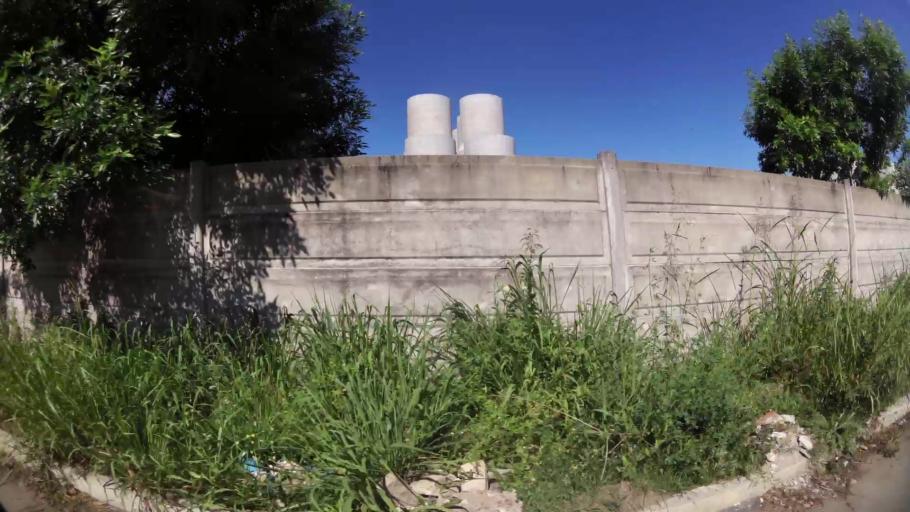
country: AR
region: Cordoba
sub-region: Departamento de Capital
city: Cordoba
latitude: -31.4077
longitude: -64.1457
